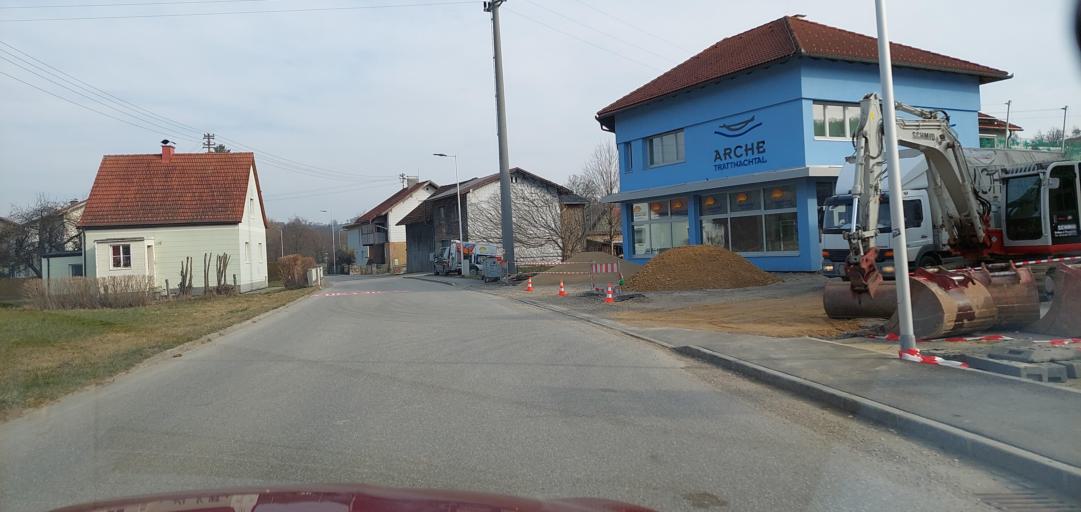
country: AT
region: Upper Austria
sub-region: Politischer Bezirk Grieskirchen
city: Grieskirchen
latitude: 48.2211
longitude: 13.8692
